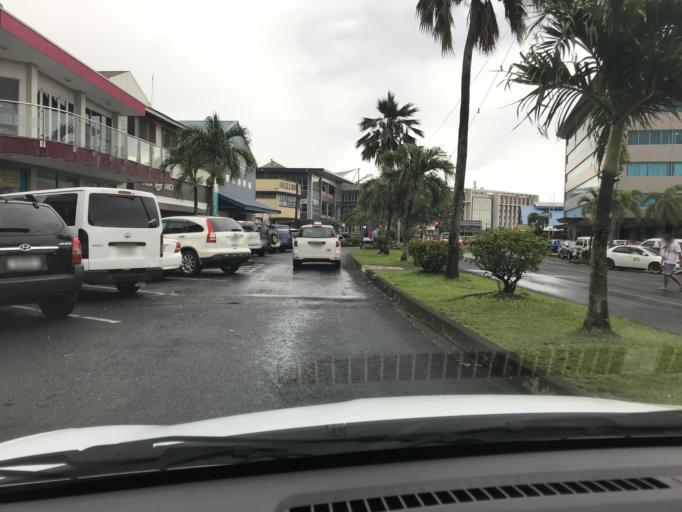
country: WS
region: Tuamasaga
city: Apia
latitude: -13.8305
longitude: -171.7697
